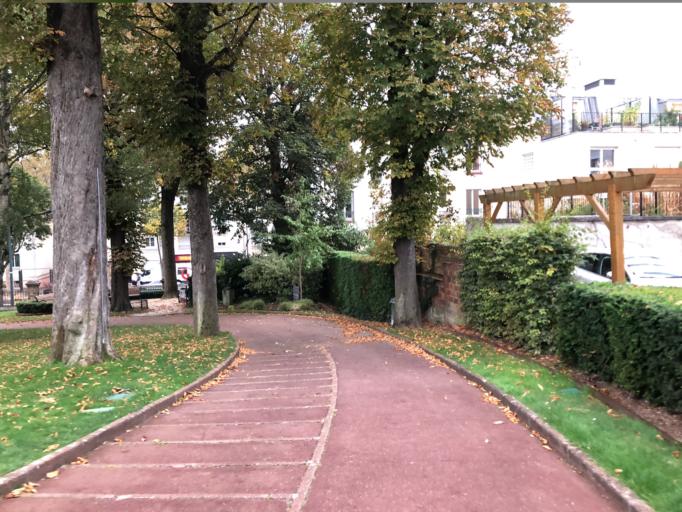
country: FR
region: Ile-de-France
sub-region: Departement des Hauts-de-Seine
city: Chaville
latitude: 48.8096
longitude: 2.1881
